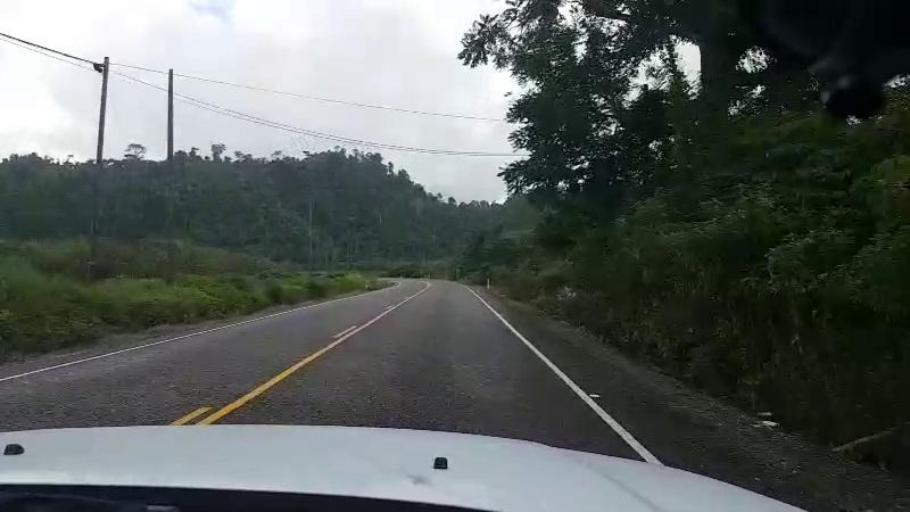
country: BZ
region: Cayo
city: Belmopan
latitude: 17.1468
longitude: -88.6990
